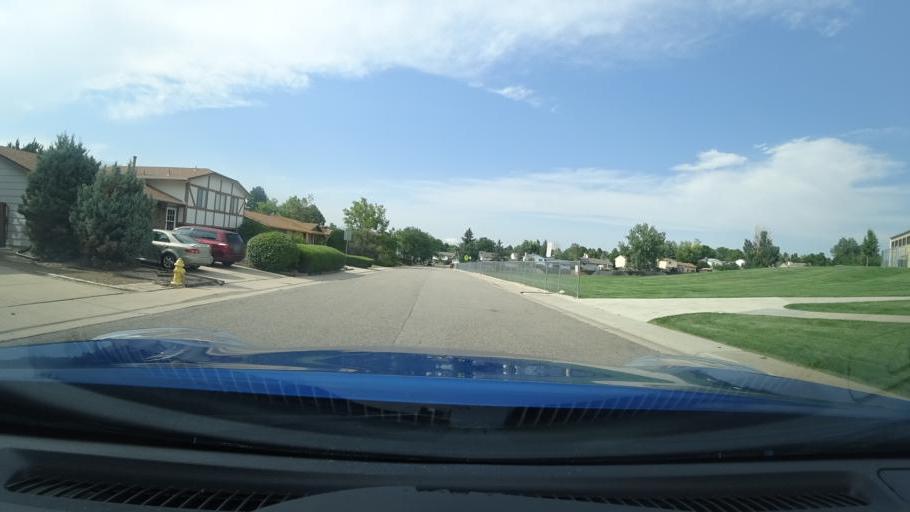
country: US
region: Colorado
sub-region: Adams County
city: Aurora
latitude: 39.6881
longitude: -104.7942
